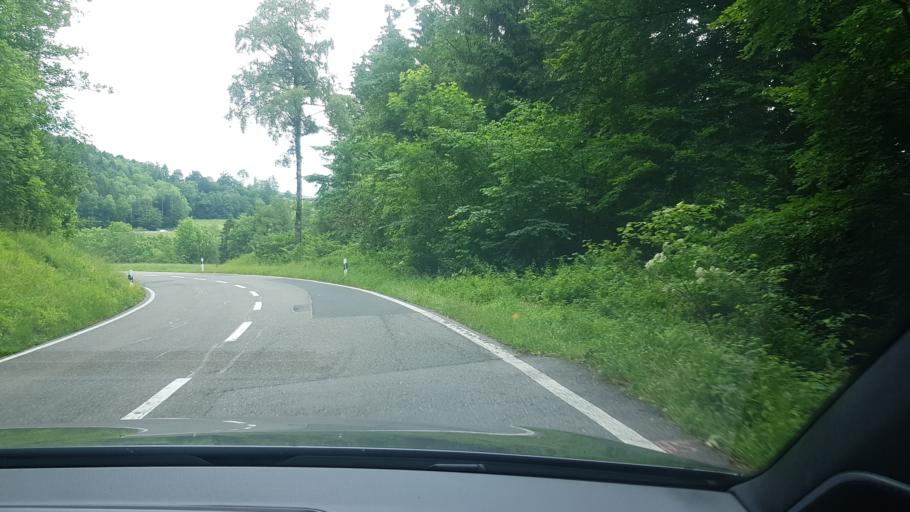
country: CH
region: Zug
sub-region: Zug
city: Baar
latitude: 47.2011
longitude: 8.5578
